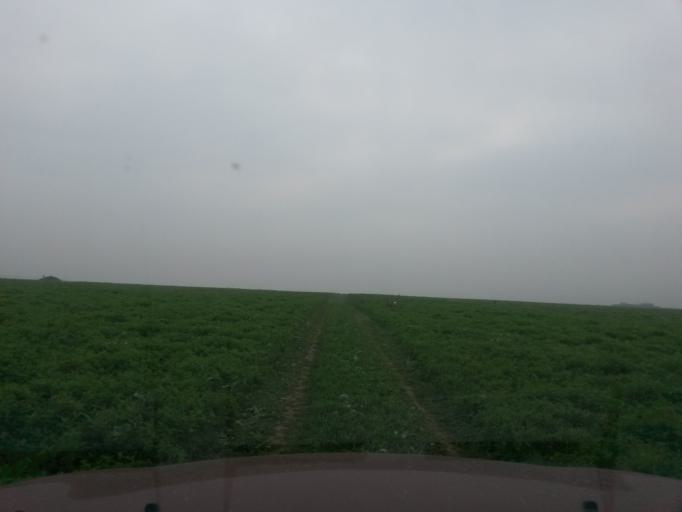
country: SK
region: Presovsky
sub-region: Okres Presov
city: Presov
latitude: 48.8890
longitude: 21.2697
